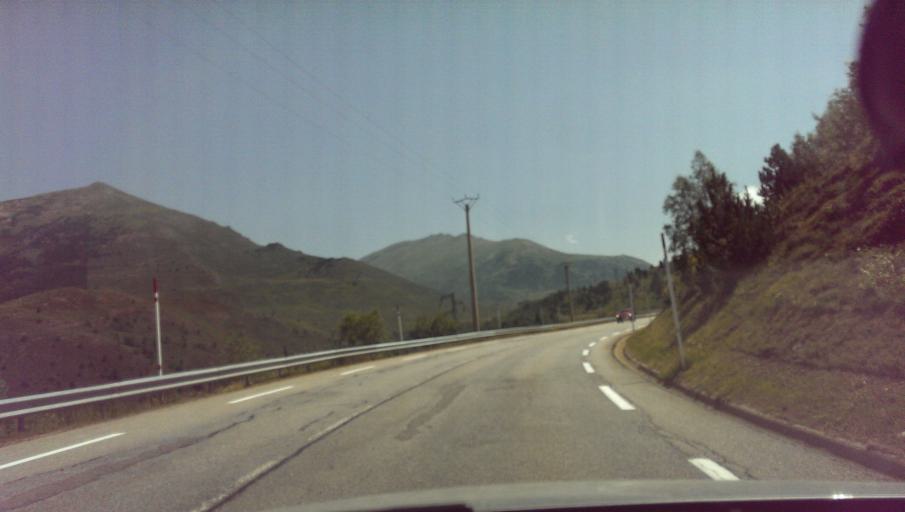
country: AD
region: Encamp
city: Pas de la Casa
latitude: 42.5676
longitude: 1.7881
